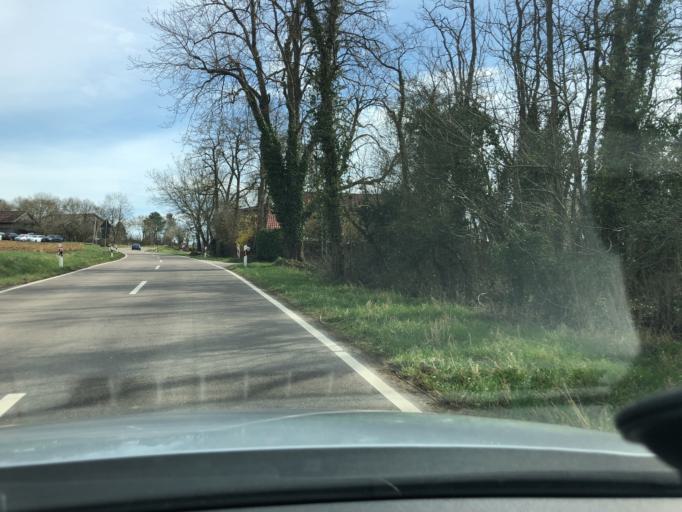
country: DE
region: Baden-Wuerttemberg
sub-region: Karlsruhe Region
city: Illingen
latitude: 48.9329
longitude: 8.9205
